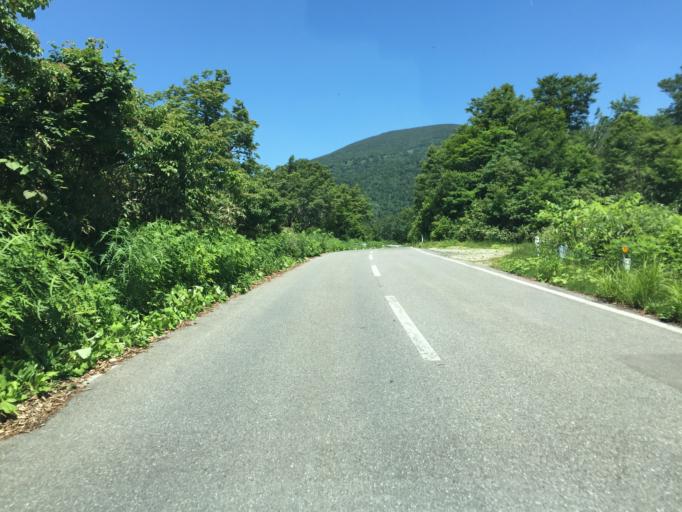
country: JP
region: Fukushima
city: Inawashiro
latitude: 37.6804
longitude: 140.2313
